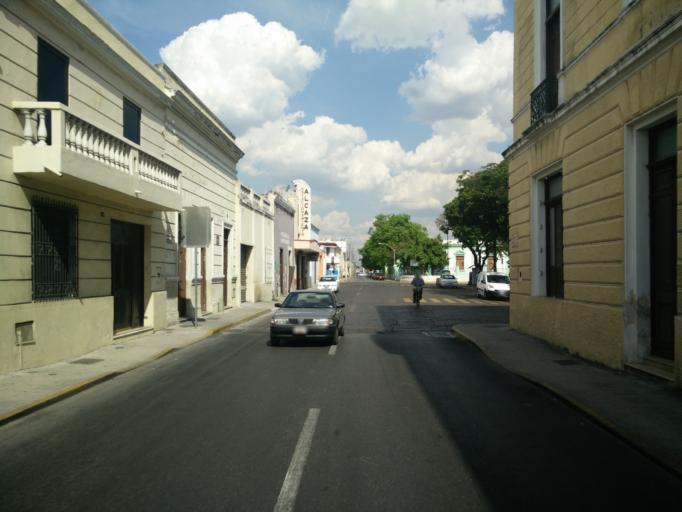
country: MX
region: Yucatan
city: Merida
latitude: 20.9690
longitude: -89.6167
